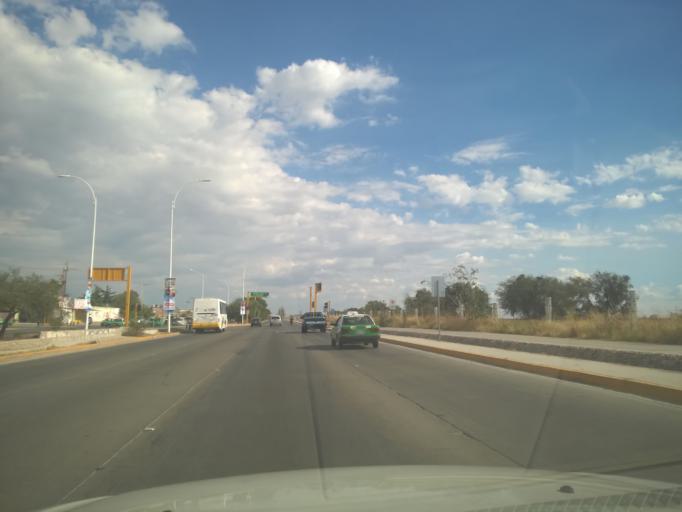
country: MX
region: Guanajuato
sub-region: Leon
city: San Jose de Duran (Los Troncoso)
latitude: 21.0727
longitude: -101.6461
